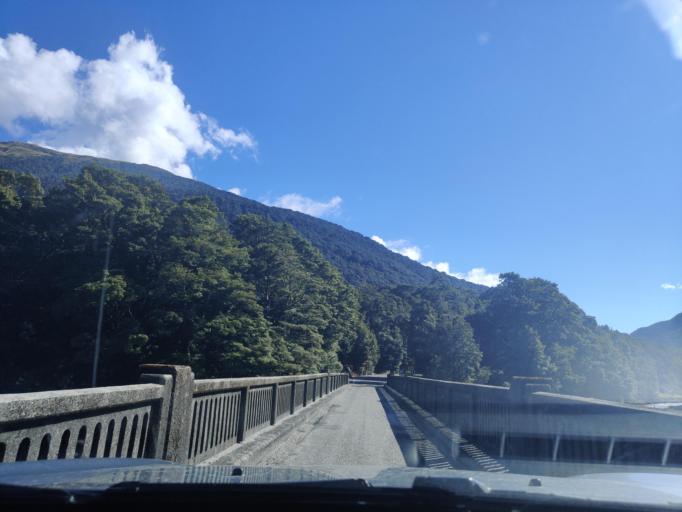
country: NZ
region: Otago
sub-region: Queenstown-Lakes District
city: Wanaka
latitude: -44.1401
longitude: 169.3290
